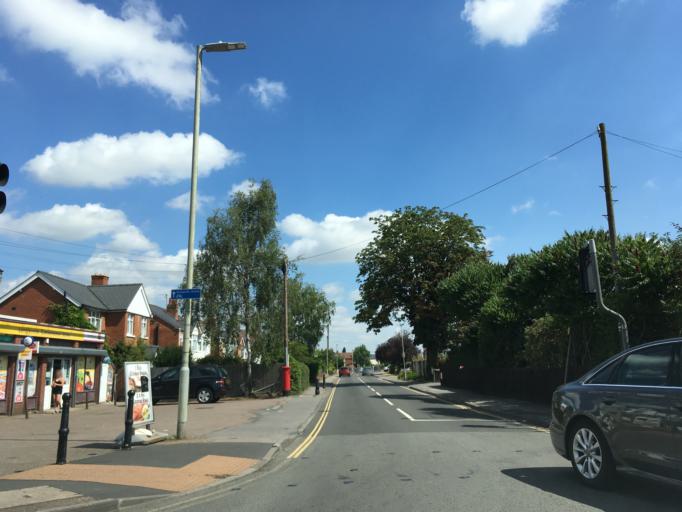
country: GB
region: England
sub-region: Gloucestershire
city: Barnwood
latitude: 51.8779
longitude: -2.2172
